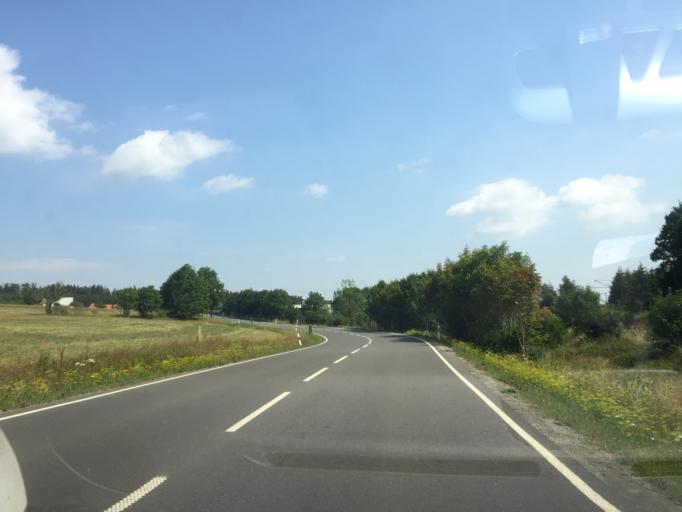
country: DE
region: Saxony-Anhalt
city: Elbingerode
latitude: 51.7643
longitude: 10.7848
